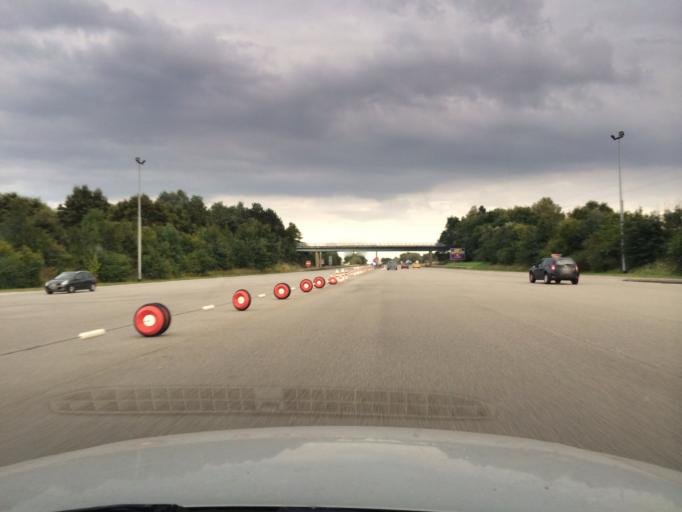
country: FR
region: Haute-Normandie
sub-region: Departement de l'Eure
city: Ande
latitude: 49.1902
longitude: 1.2333
